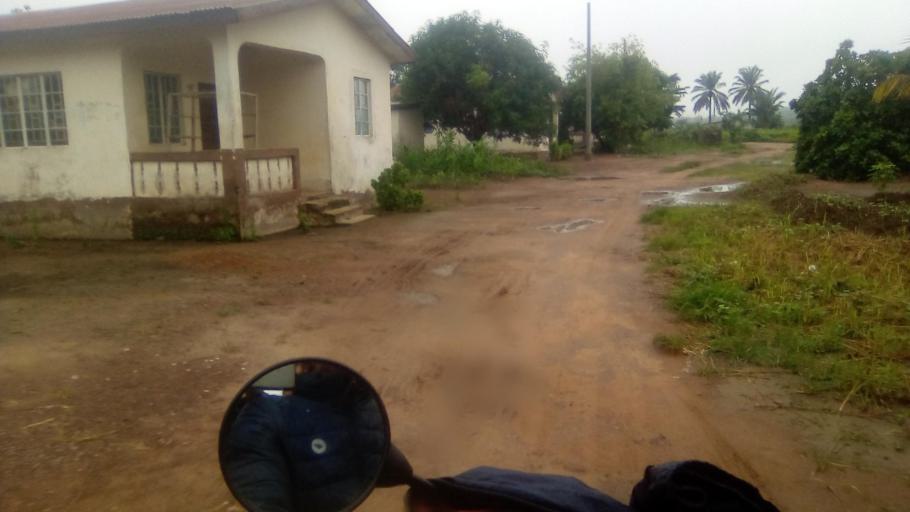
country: SL
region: Southern Province
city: Moyamba
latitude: 8.1472
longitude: -12.4390
